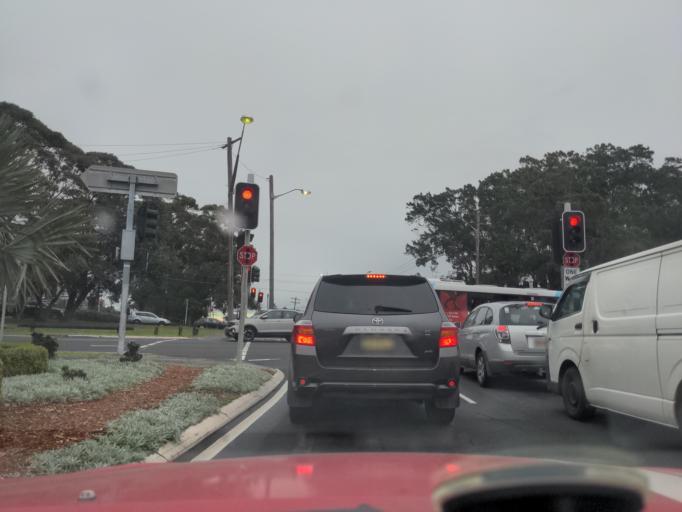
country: AU
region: New South Wales
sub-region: Randwick
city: Maroubra
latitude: -33.9463
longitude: 151.2409
